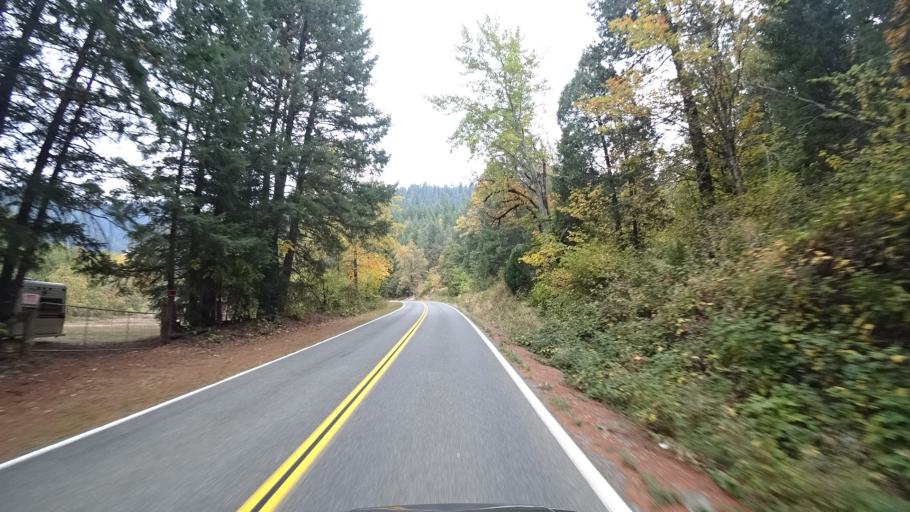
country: US
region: California
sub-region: Siskiyou County
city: Happy Camp
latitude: 41.8815
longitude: -123.4220
